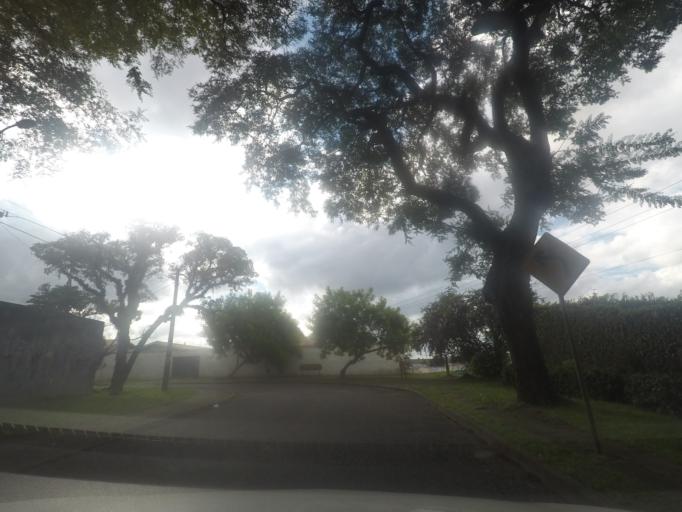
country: BR
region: Parana
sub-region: Pinhais
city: Pinhais
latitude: -25.4547
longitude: -49.2253
